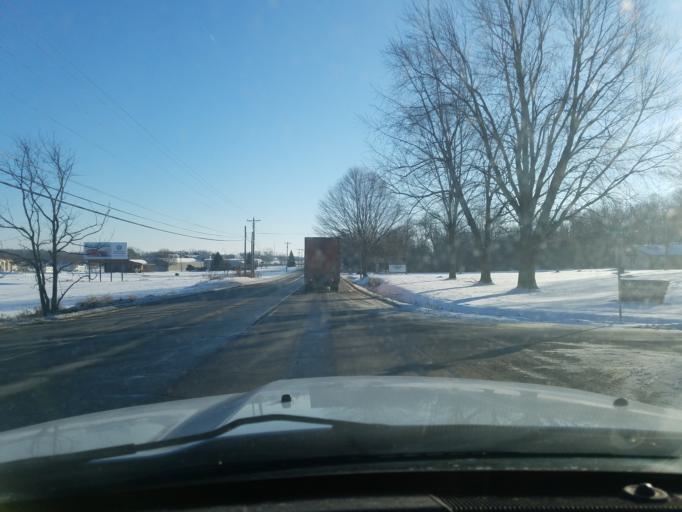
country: US
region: Indiana
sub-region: Noble County
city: Kendallville
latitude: 41.4524
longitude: -85.3044
